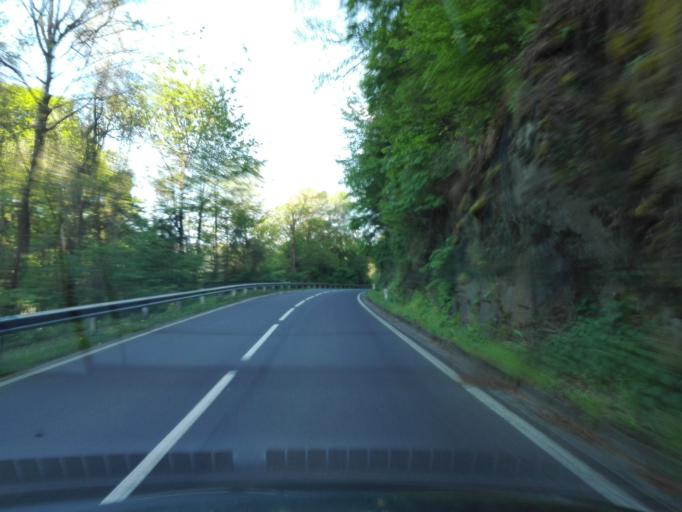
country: AT
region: Upper Austria
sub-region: Politischer Bezirk Rohrbach
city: Pfarrkirchen im Muehlkreis
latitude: 48.4668
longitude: 13.7806
